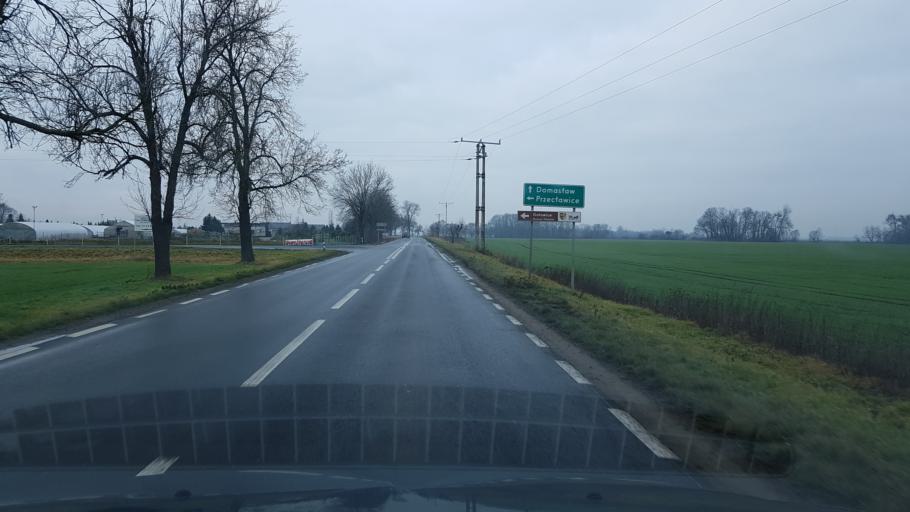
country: PL
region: Lower Silesian Voivodeship
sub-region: Powiat wroclawski
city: Zorawina
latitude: 50.9882
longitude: 17.0047
